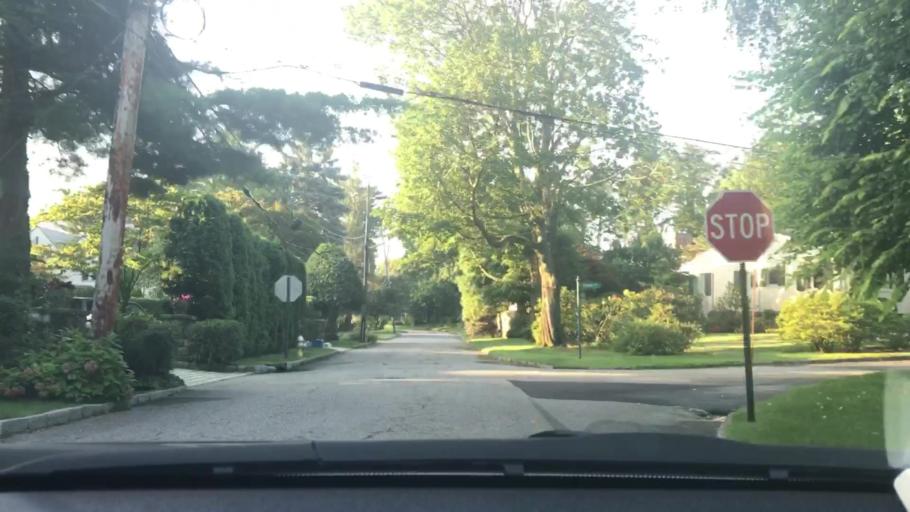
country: US
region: New York
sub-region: Westchester County
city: Bronxville
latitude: 40.9374
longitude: -73.8160
